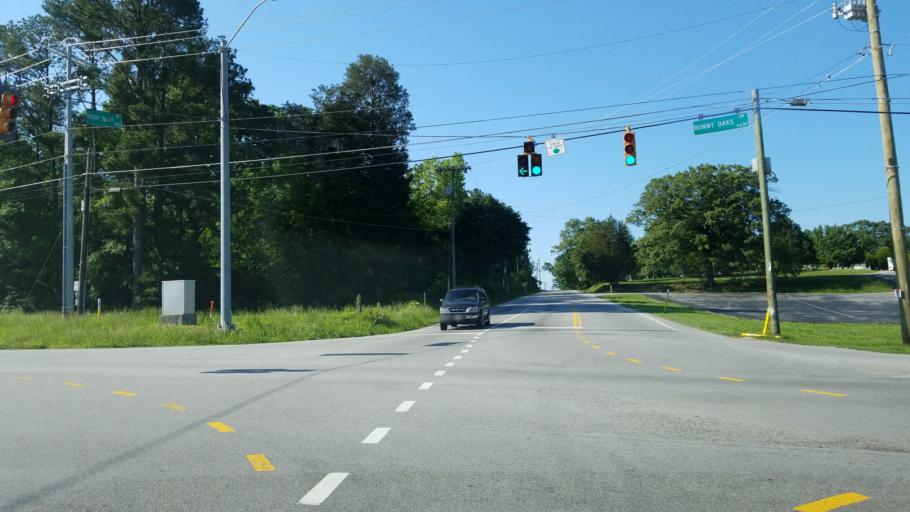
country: US
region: Tennessee
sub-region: Hamilton County
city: Harrison
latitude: 35.0716
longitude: -85.1564
